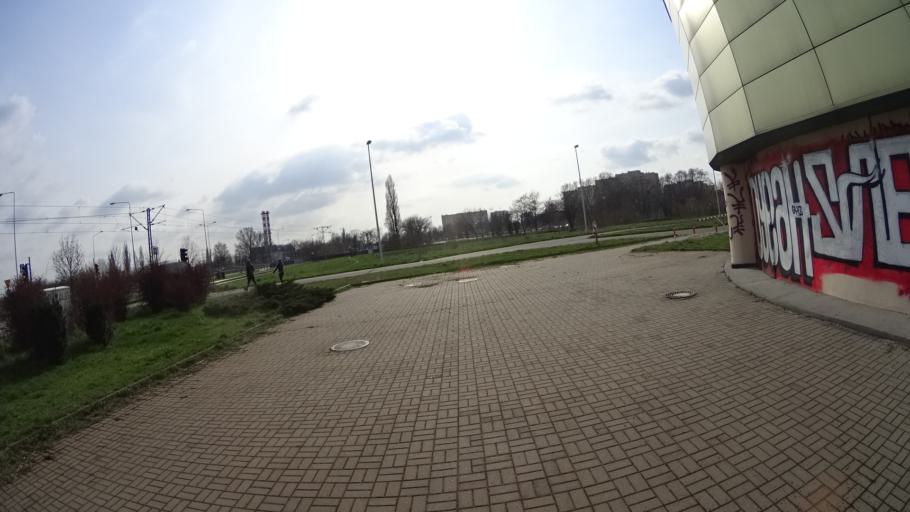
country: PL
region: Masovian Voivodeship
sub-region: Warszawa
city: Bemowo
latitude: 52.2230
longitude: 20.9262
